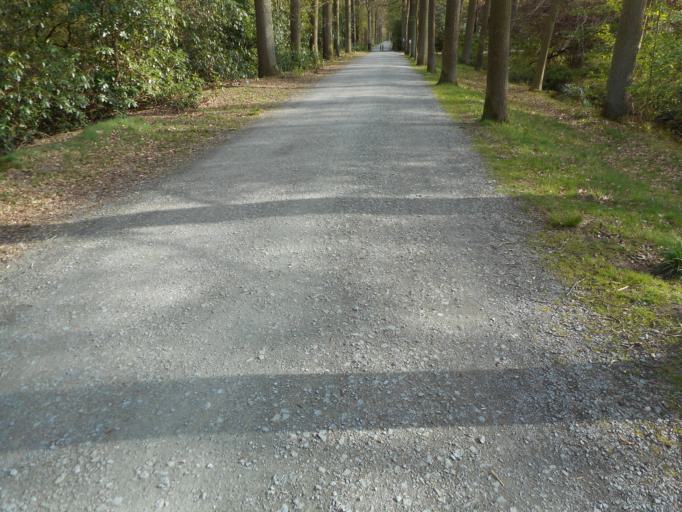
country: BE
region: Flanders
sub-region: Provincie Antwerpen
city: Brasschaat
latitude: 51.2754
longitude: 4.4843
